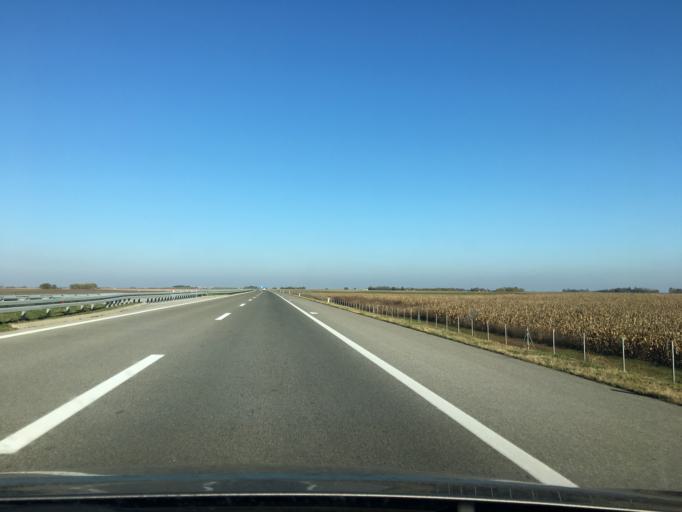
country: RS
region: Autonomna Pokrajina Vojvodina
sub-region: Severnobacki Okrug
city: Mali Igos
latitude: 45.7674
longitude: 19.7010
